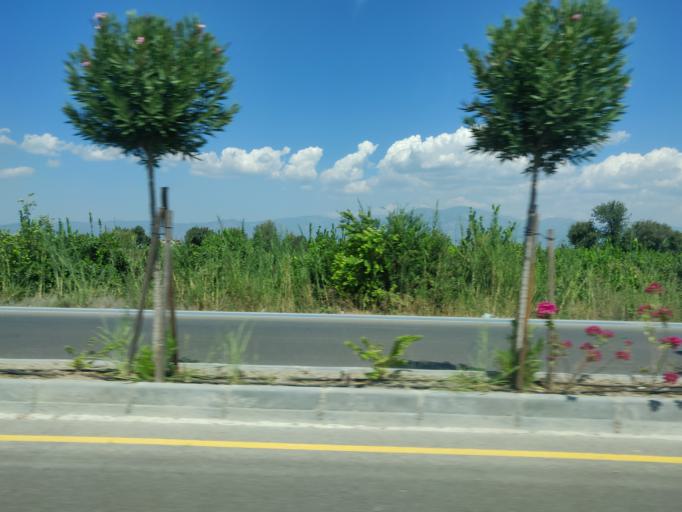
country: TR
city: Dalyan
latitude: 36.8396
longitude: 28.6580
